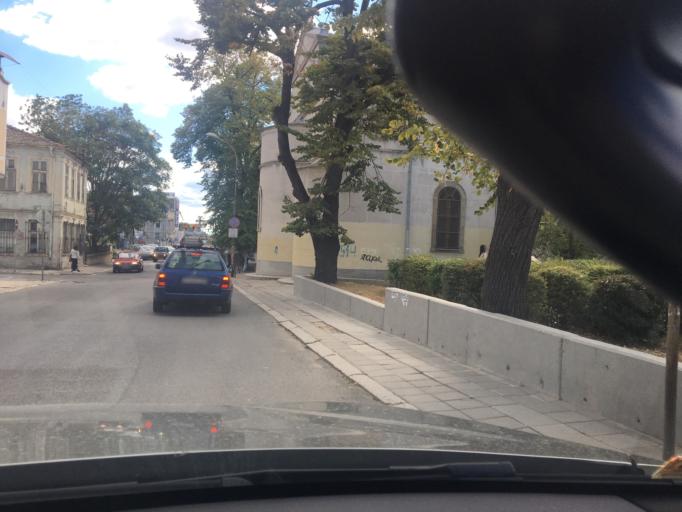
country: BG
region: Burgas
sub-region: Obshtina Burgas
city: Burgas
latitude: 42.4927
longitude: 27.4753
